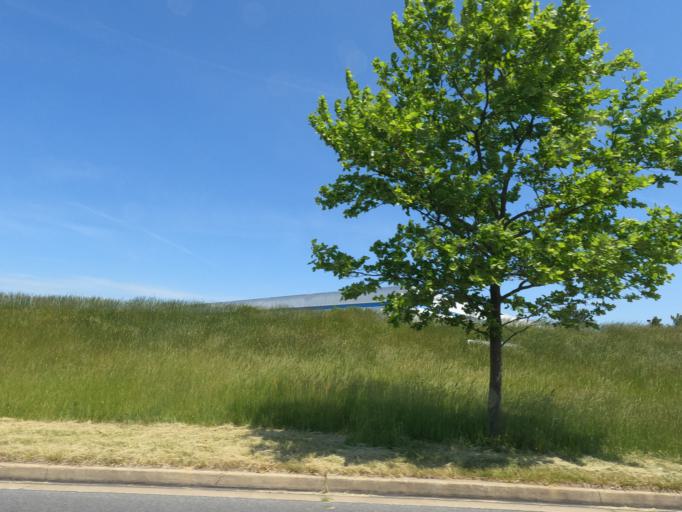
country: US
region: Maryland
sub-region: Howard County
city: Savage
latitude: 39.1763
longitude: -76.8150
